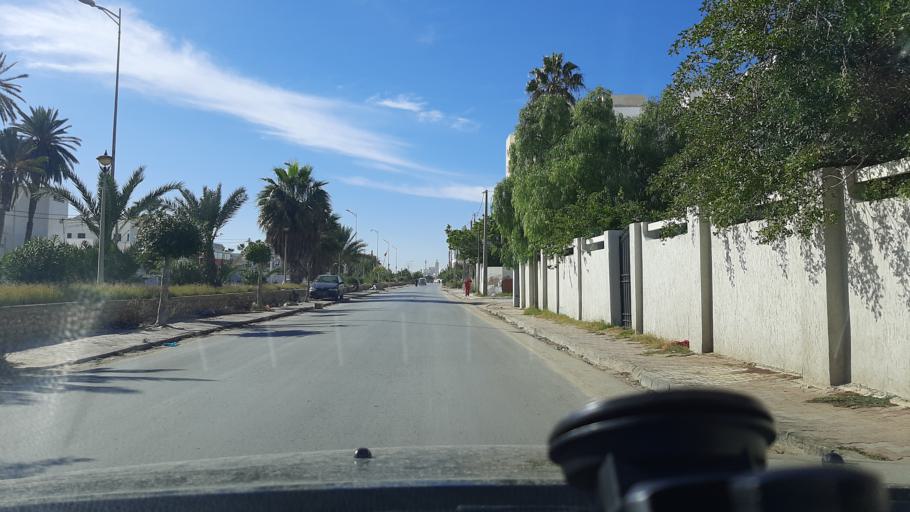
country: TN
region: Safaqis
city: Sfax
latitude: 34.7252
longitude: 10.7392
